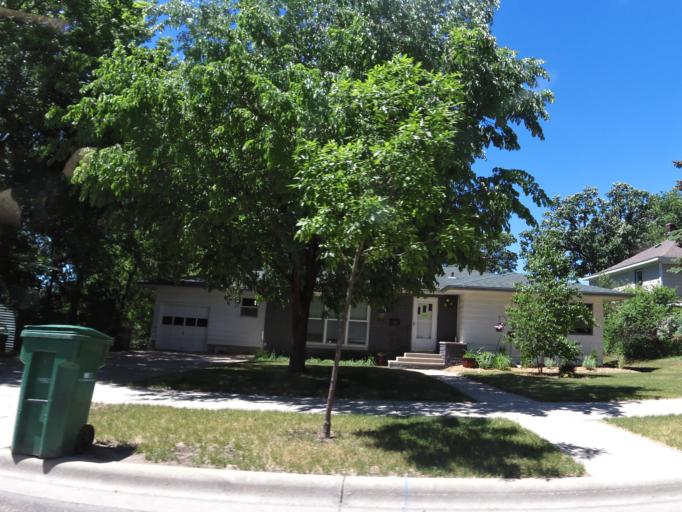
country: US
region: Minnesota
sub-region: Becker County
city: Detroit Lakes
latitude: 46.8079
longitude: -95.8490
